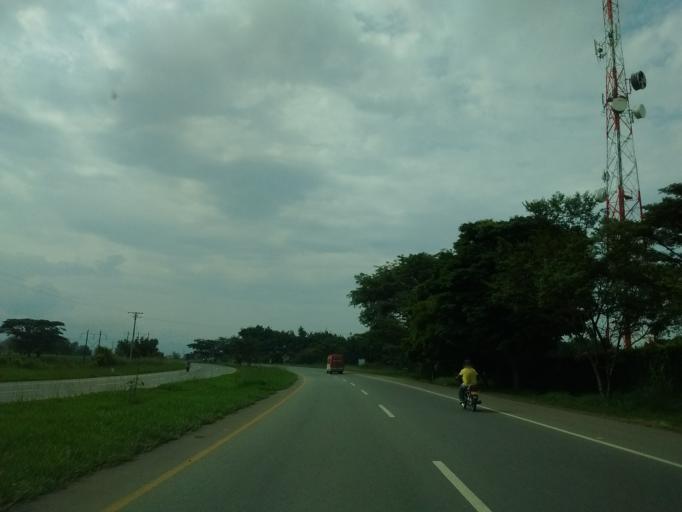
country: CO
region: Cauca
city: Santander de Quilichao
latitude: 3.0795
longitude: -76.4751
